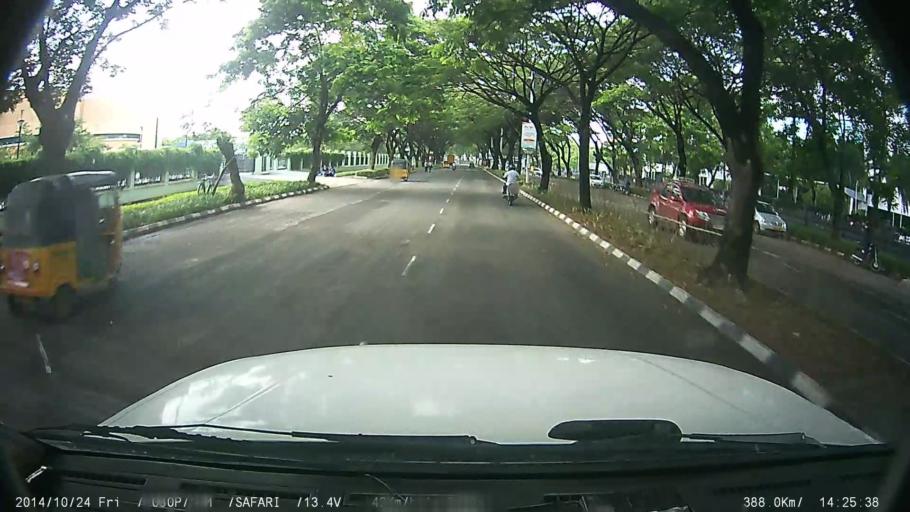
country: IN
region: Tamil Nadu
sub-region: Kancheepuram
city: Singapperumalkovil
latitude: 12.7369
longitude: 80.0054
